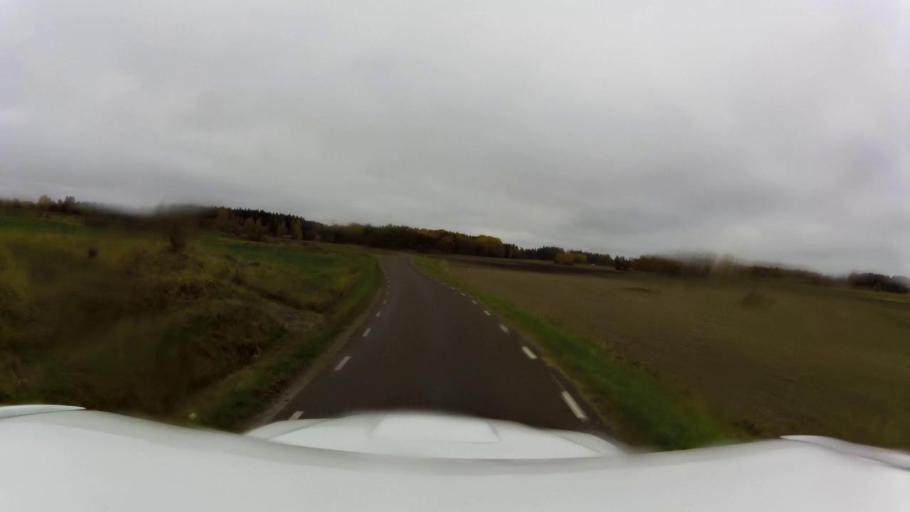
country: SE
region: OEstergoetland
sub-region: Linkopings Kommun
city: Linghem
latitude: 58.4642
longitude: 15.7820
